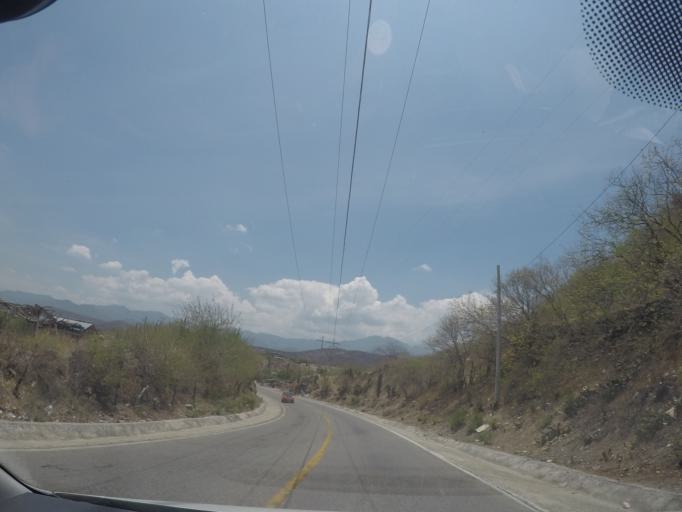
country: MX
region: Oaxaca
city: Magdalena Tequisistlan
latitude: 16.4144
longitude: -95.5964
